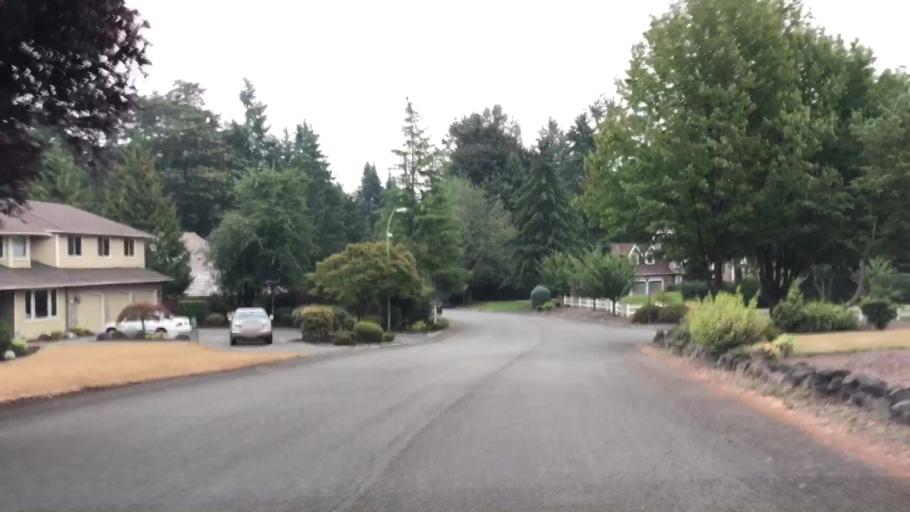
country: US
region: Washington
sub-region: King County
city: Cottage Lake
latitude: 47.7387
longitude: -122.1016
